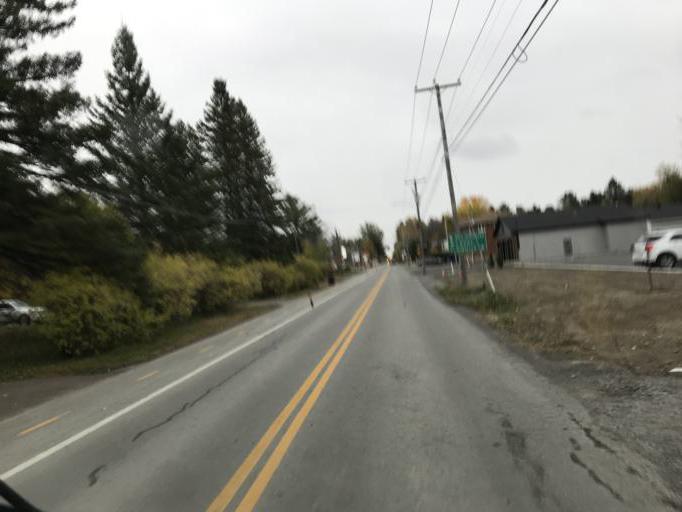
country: CA
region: Quebec
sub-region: Lanaudiere
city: Lorraine
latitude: 45.6851
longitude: -73.7906
